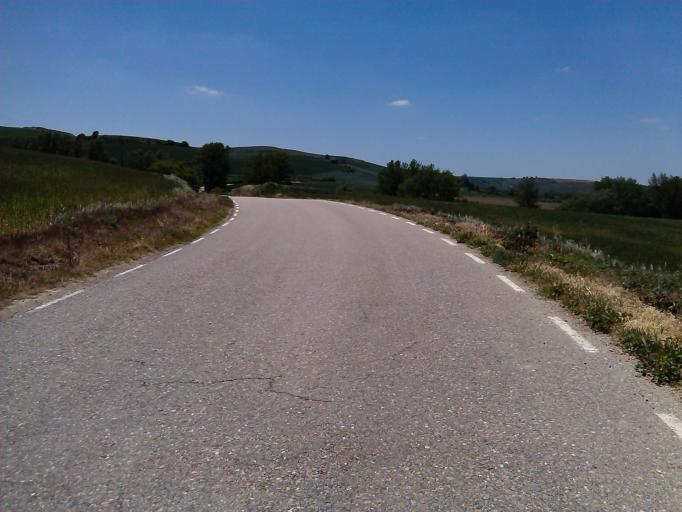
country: ES
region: Castille and Leon
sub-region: Provincia de Burgos
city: Arraya de Oca
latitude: 42.4232
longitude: -3.3968
